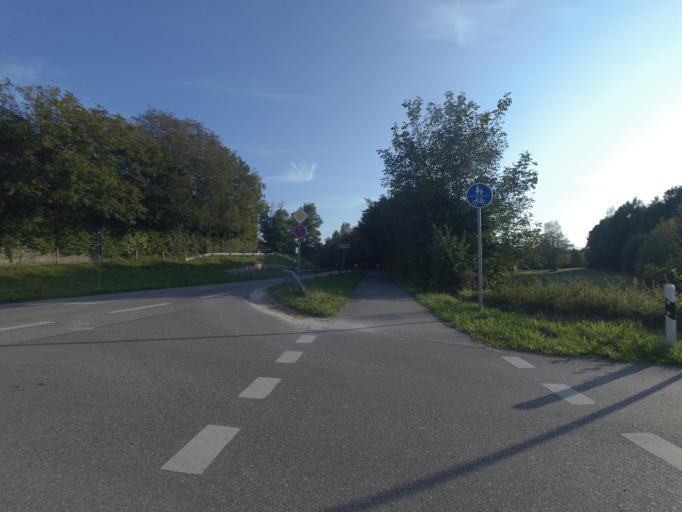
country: DE
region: Bavaria
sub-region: Upper Bavaria
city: Laufen
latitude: 47.9135
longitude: 12.9147
